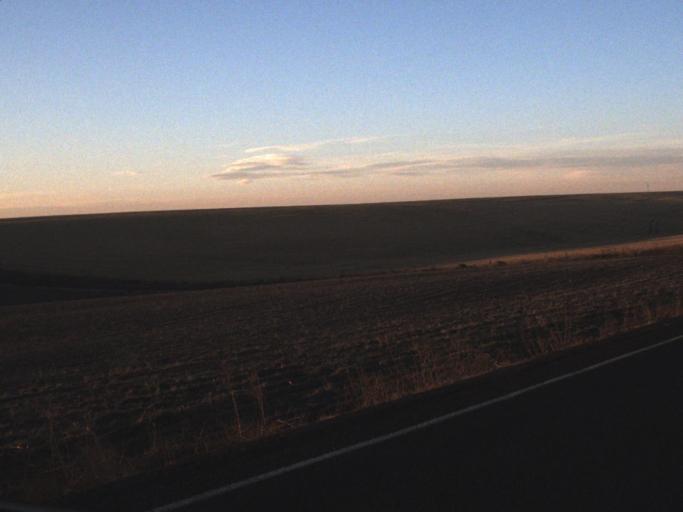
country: US
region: Washington
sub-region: Adams County
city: Ritzville
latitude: 47.0569
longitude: -118.6630
